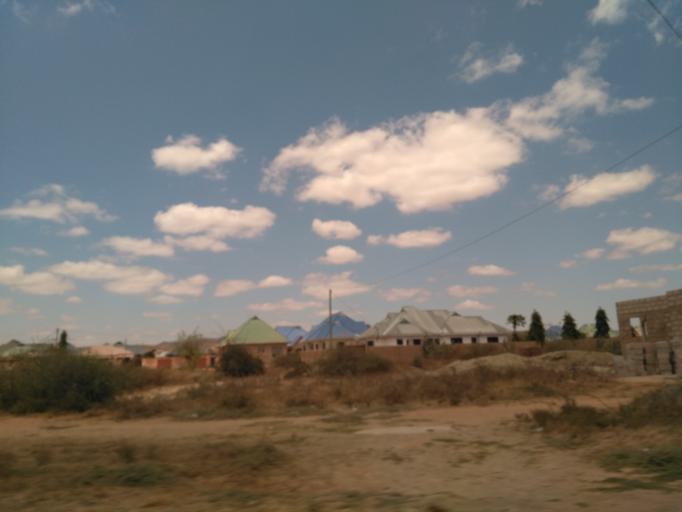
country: TZ
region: Dodoma
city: Kisasa
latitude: -6.1685
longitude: 35.7997
